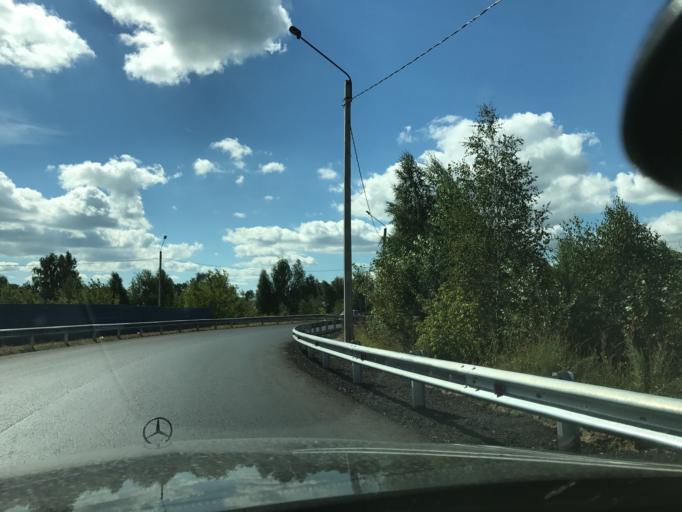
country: RU
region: Nizjnij Novgorod
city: Gorbatovka
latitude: 56.2204
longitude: 43.7496
